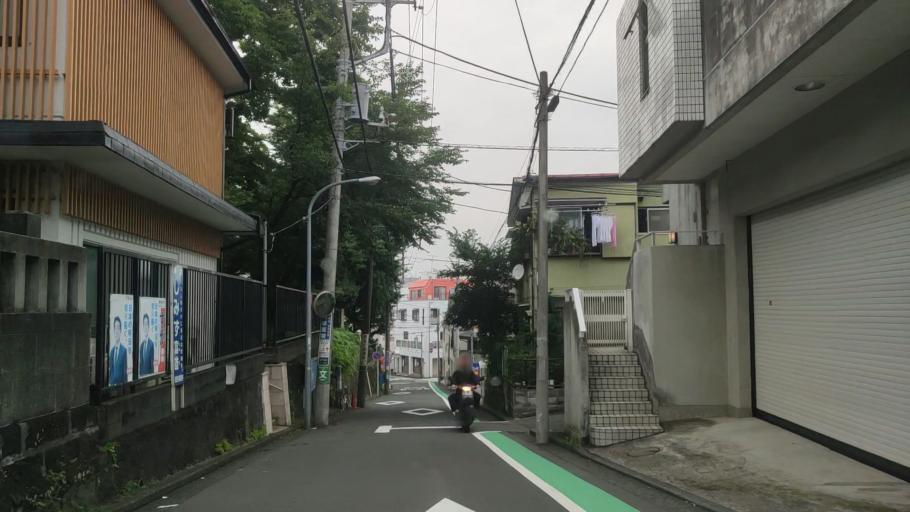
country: JP
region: Kanagawa
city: Yokohama
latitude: 35.4512
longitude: 139.6162
